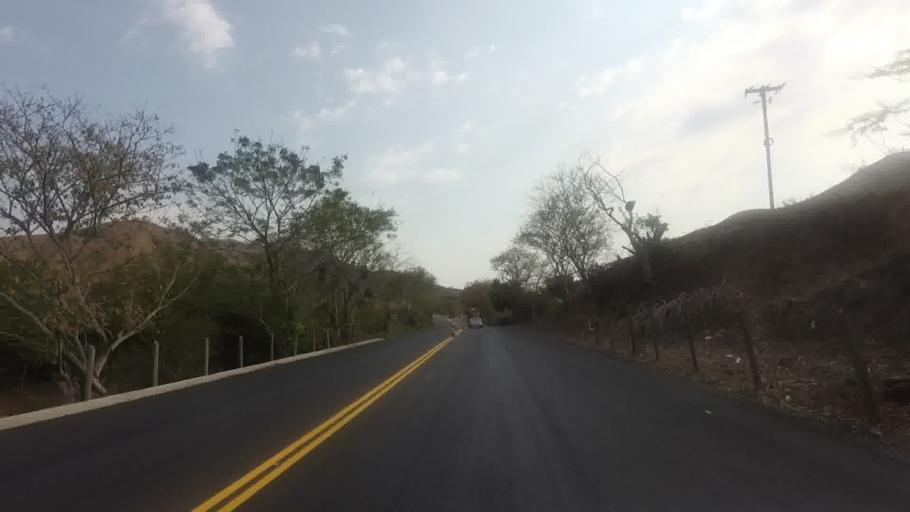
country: BR
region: Rio de Janeiro
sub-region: Bom Jesus Do Itabapoana
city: Bom Jesus do Itabapoana
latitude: -21.2065
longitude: -41.7241
